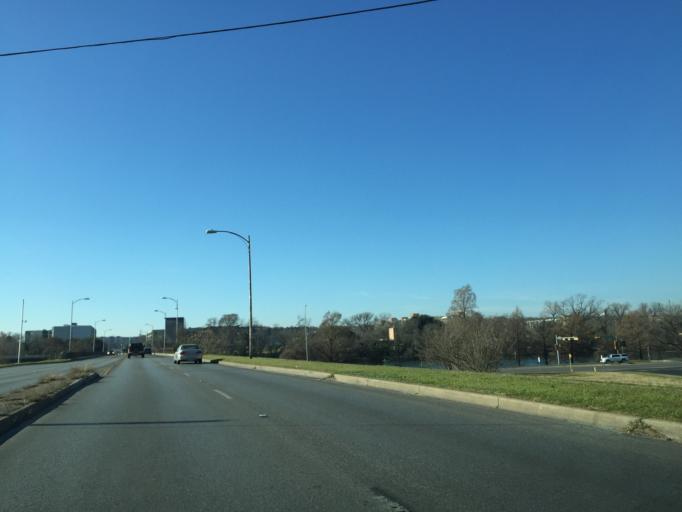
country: US
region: Texas
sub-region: Travis County
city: Austin
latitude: 30.2676
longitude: -97.7558
